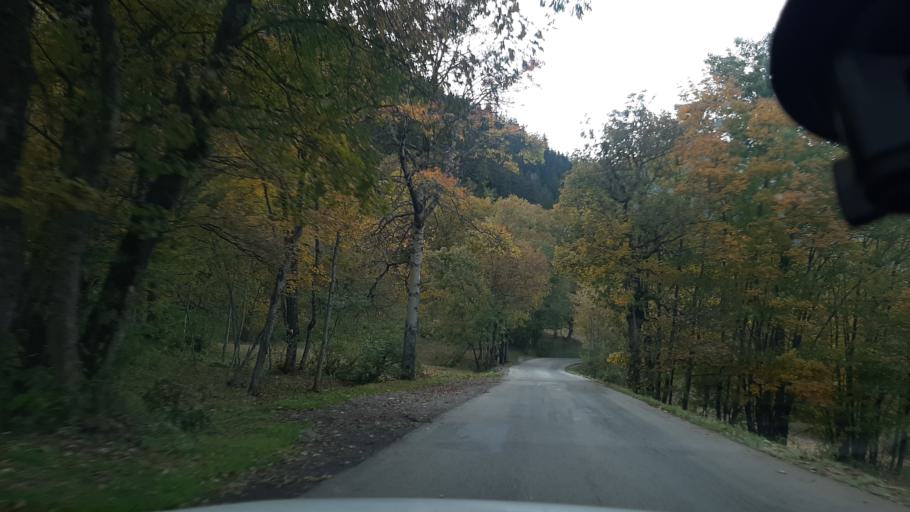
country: FR
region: Rhone-Alpes
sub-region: Departement de la Savoie
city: Villargondran
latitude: 45.1975
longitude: 6.3244
